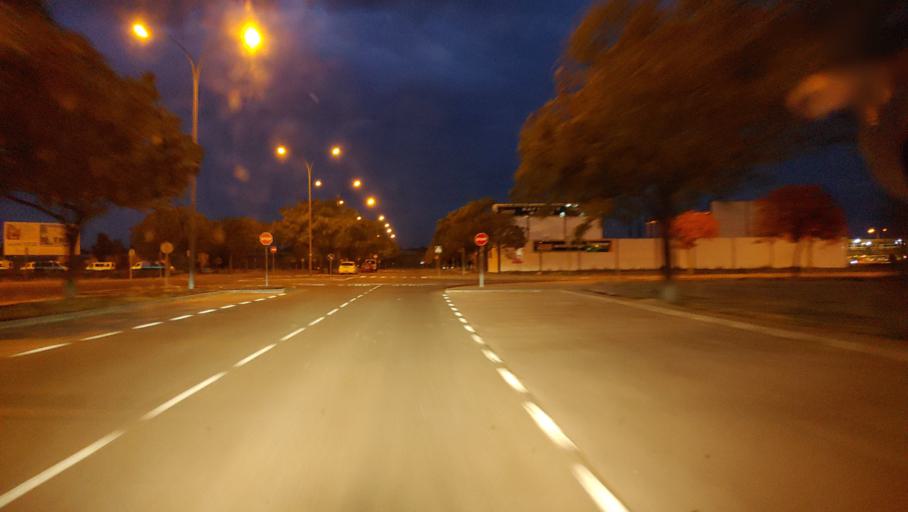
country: ES
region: Castille-La Mancha
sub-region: Provincia de Ciudad Real
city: Ciudad Real
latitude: 38.9844
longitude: -3.9077
